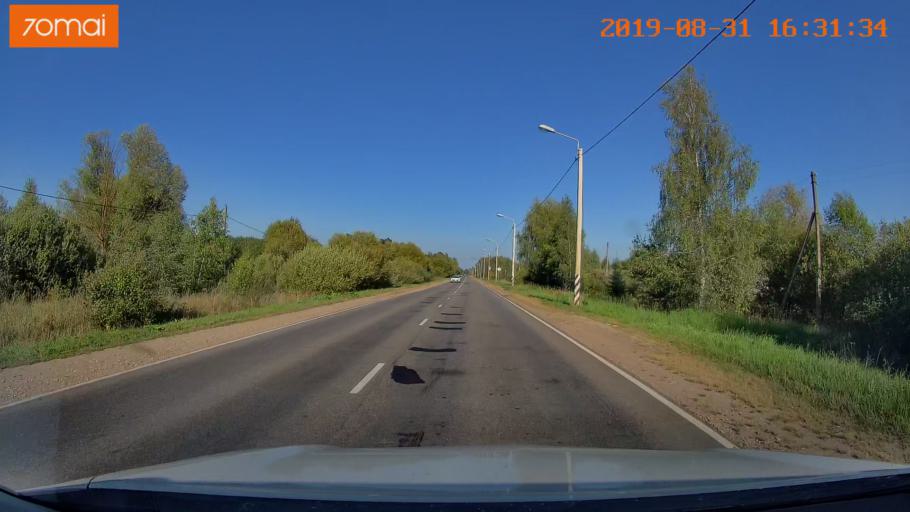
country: RU
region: Kaluga
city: Babynino
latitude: 54.5156
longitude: 35.8539
